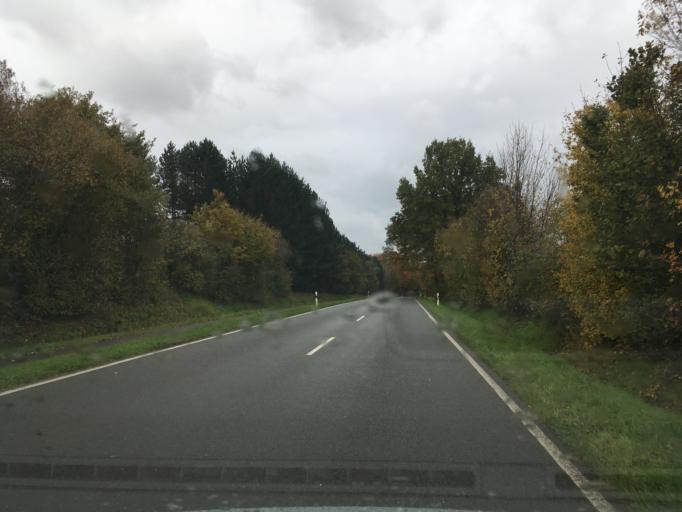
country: DE
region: North Rhine-Westphalia
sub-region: Regierungsbezirk Munster
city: Klein Reken
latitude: 51.8171
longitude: 7.1006
